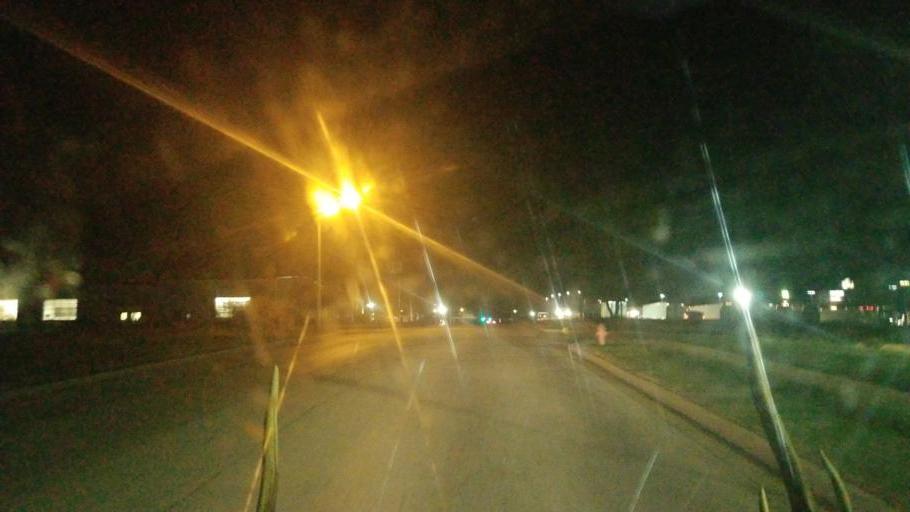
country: US
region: Missouri
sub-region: Jackson County
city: Oak Grove
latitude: 39.0128
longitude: -94.1250
